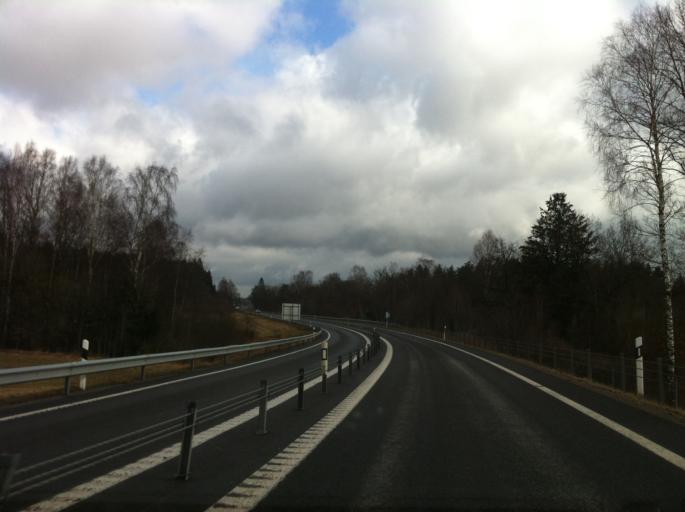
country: SE
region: Halland
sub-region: Halmstads Kommun
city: Oskarstrom
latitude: 56.8515
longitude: 13.0280
